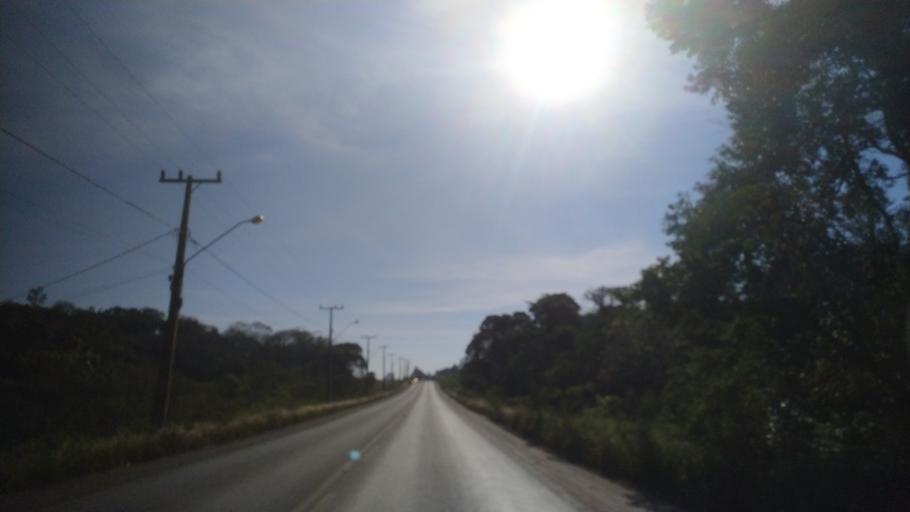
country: BR
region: Santa Catarina
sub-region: Chapeco
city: Chapeco
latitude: -27.1210
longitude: -52.6335
